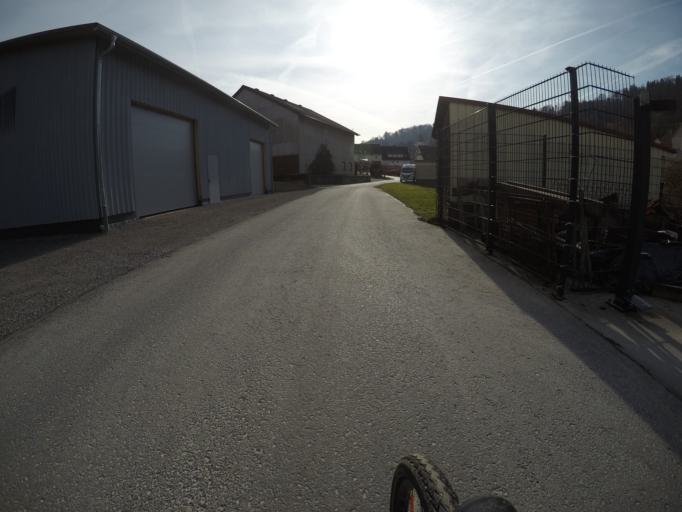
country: DE
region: Baden-Wuerttemberg
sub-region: Karlsruhe Region
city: Wildberg
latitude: 48.6228
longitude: 8.7754
